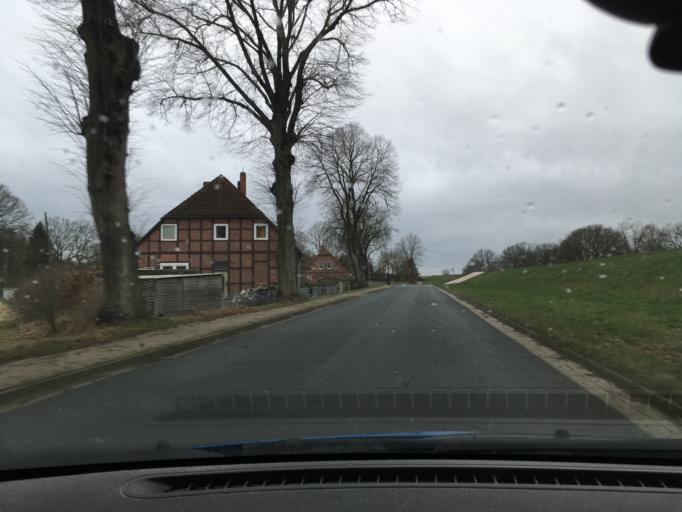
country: DE
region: Schleswig-Holstein
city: Lanze
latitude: 53.3679
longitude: 10.6269
